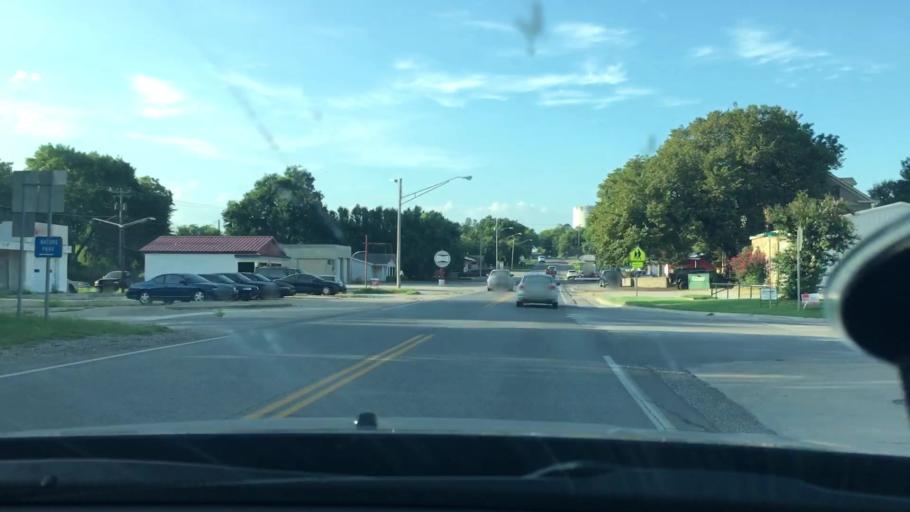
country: US
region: Oklahoma
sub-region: Garvin County
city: Pauls Valley
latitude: 34.7319
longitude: -97.2132
